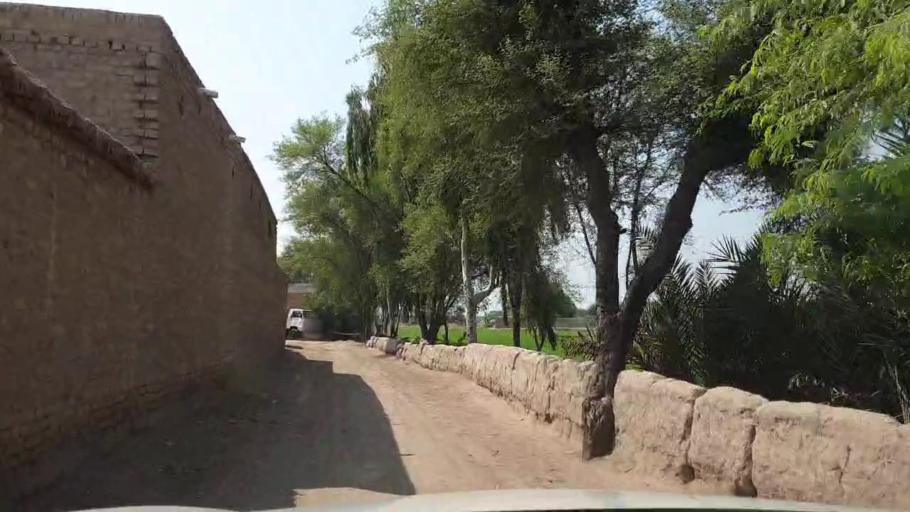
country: PK
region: Sindh
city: Ratodero
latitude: 27.8361
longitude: 68.2871
